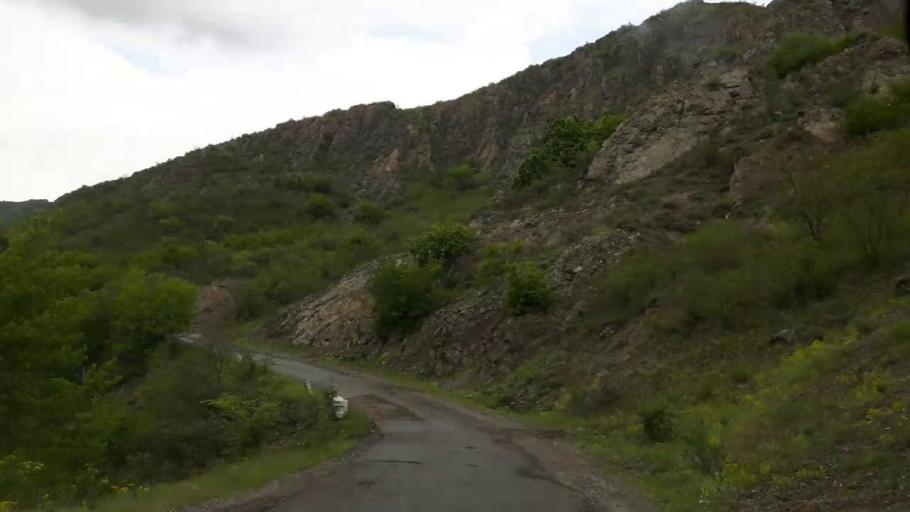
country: GE
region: Shida Kartli
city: Gori
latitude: 41.8999
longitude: 44.0555
